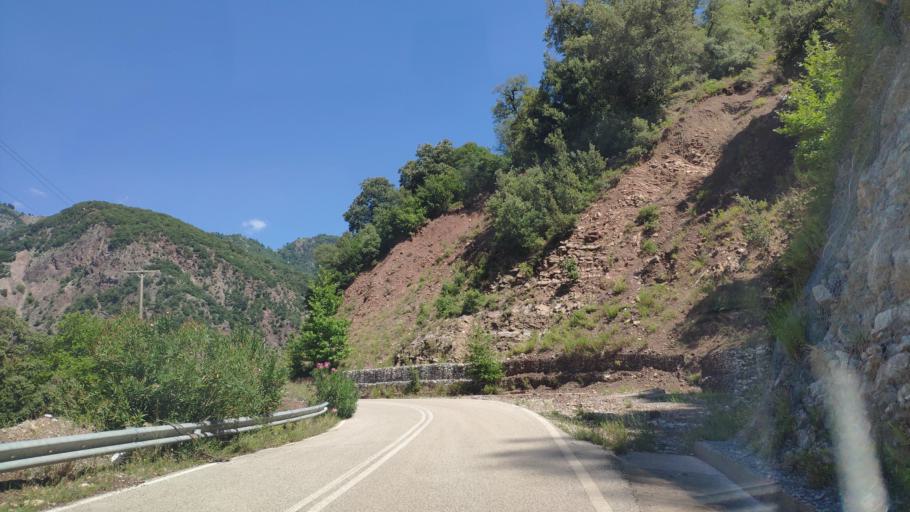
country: GR
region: Central Greece
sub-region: Nomos Evrytanias
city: Kerasochori
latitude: 39.0431
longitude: 21.5966
